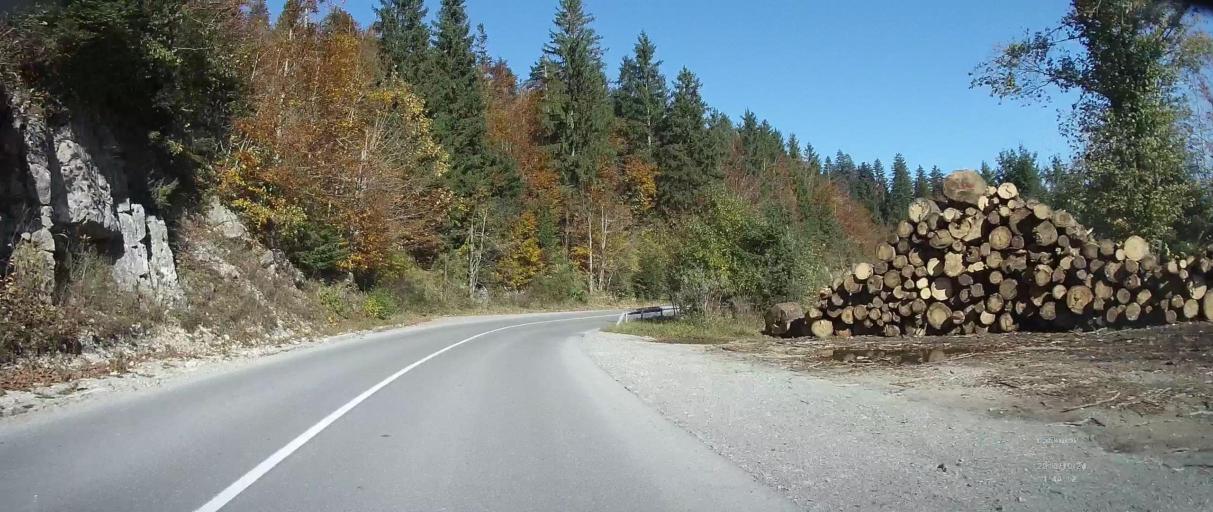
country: SI
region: Osilnica
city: Osilnica
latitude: 45.4383
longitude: 14.7083
